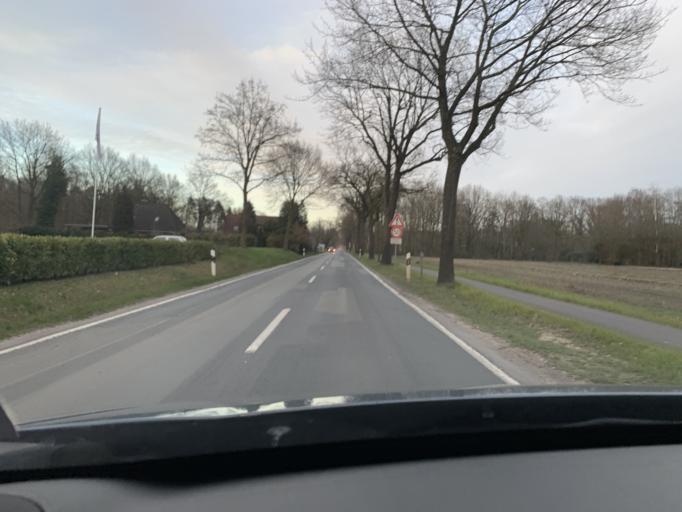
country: DE
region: Lower Saxony
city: Apen
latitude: 53.1937
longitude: 7.8711
